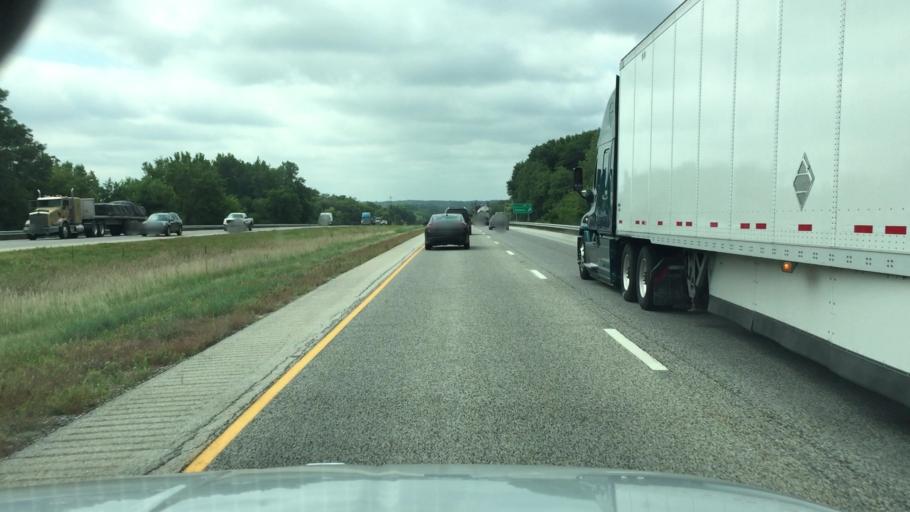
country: US
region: Illinois
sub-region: Henry County
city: Colona
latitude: 41.4927
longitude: -90.3389
